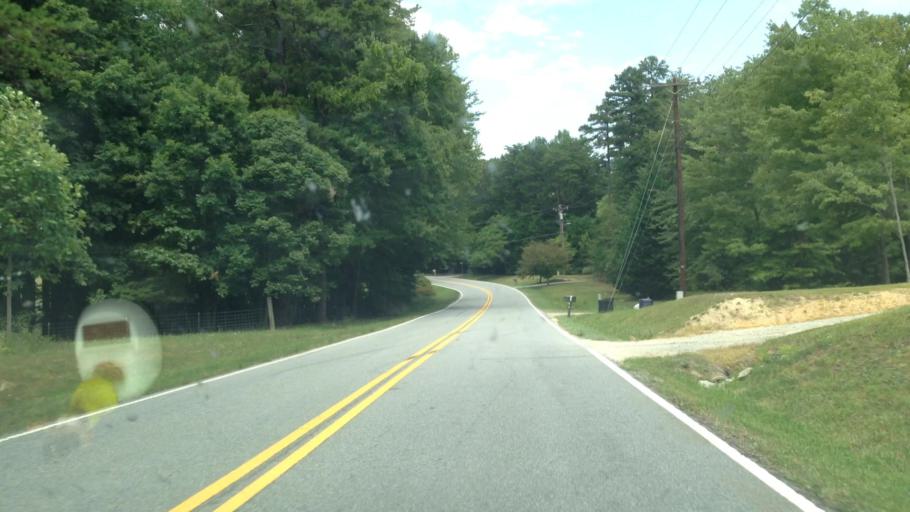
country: US
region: North Carolina
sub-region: Forsyth County
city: Walkertown
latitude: 36.2291
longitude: -80.1122
